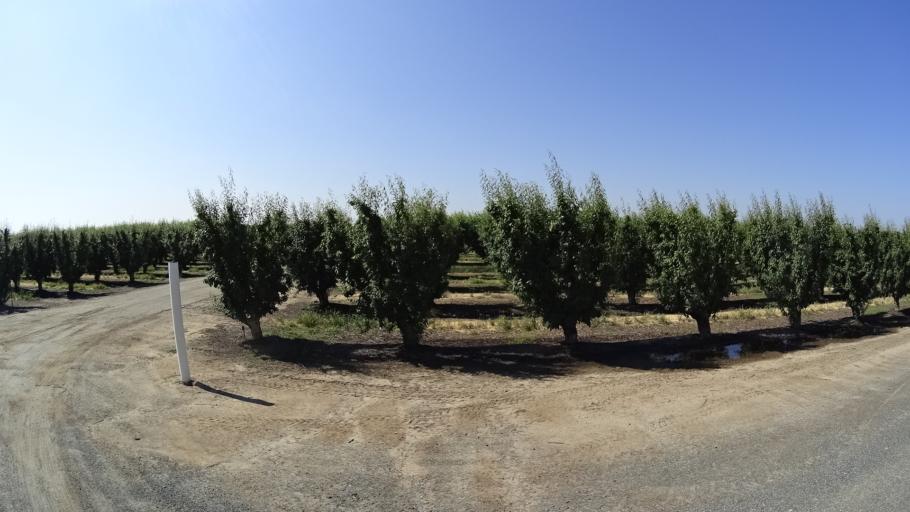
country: US
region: California
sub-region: Fresno County
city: Kingsburg
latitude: 36.4304
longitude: -119.5696
